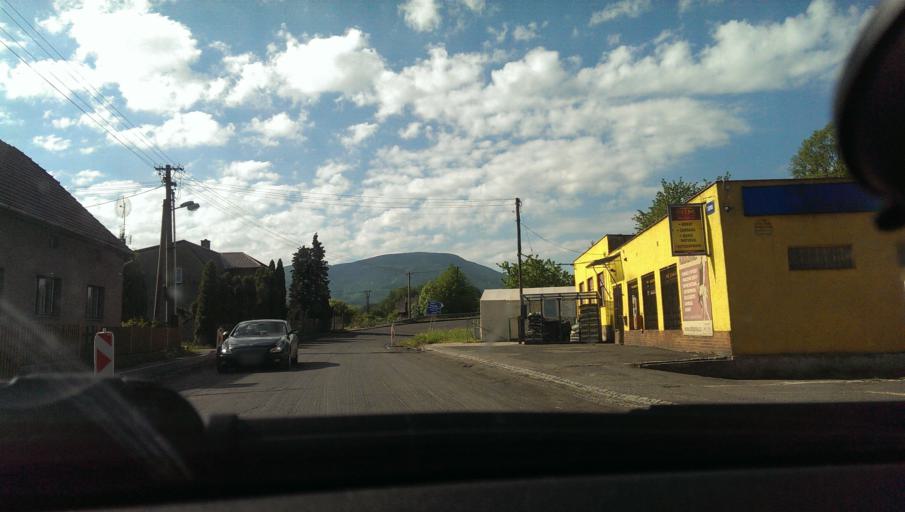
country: CZ
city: Frydlant nad Ostravici
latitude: 49.5726
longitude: 18.3601
